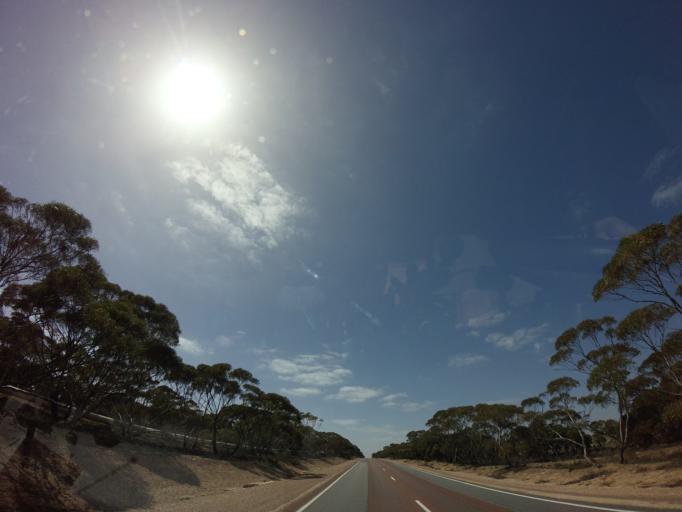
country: AU
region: South Australia
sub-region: Kimba
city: Caralue
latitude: -33.0945
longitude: 135.5158
